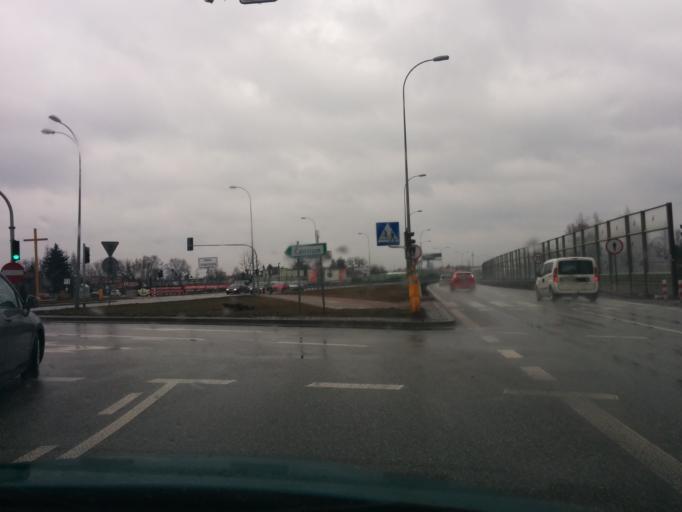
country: PL
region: Masovian Voivodeship
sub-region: Powiat legionowski
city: Jablonna
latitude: 52.3633
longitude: 20.9355
